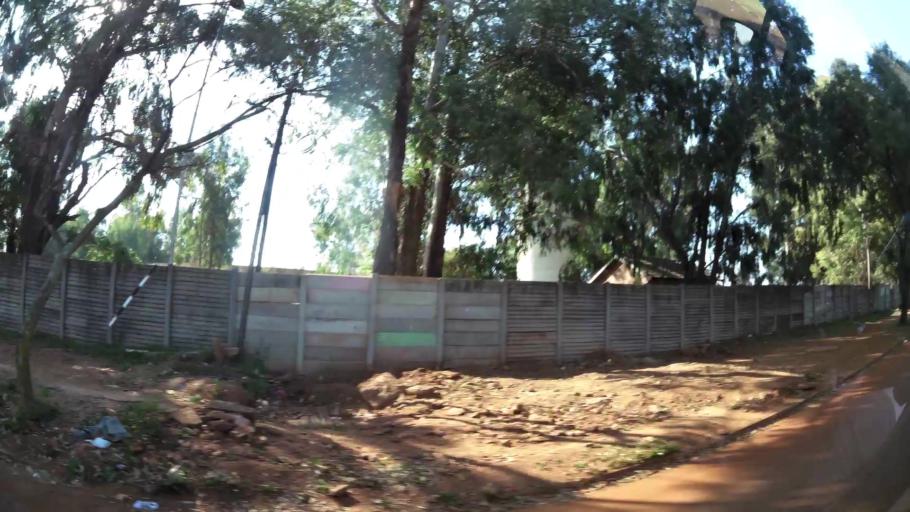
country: ZA
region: Gauteng
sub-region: West Rand District Municipality
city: Randfontein
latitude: -26.1657
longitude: 27.7028
